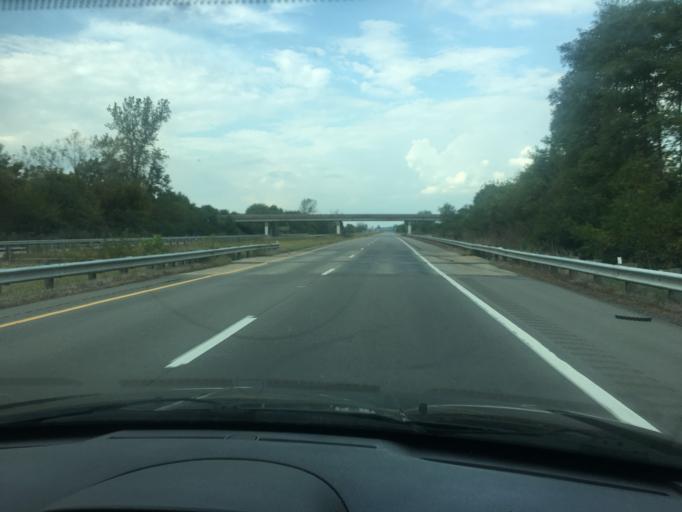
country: US
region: Ohio
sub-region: Clark County
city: Northridge
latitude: 39.9731
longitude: -83.8165
